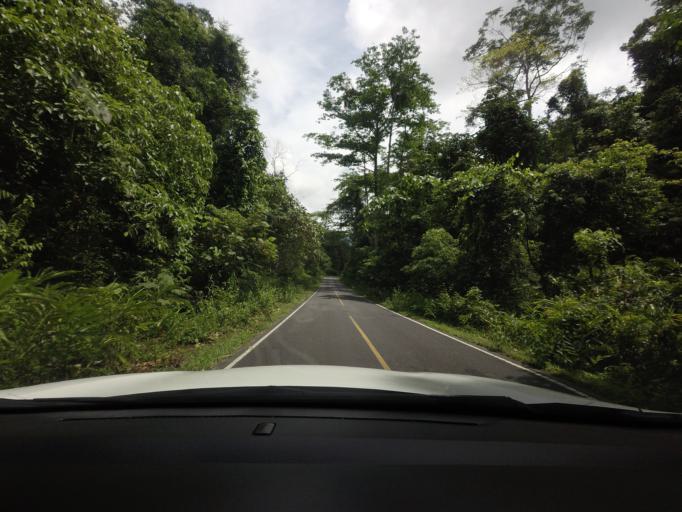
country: TH
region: Nakhon Nayok
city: Pak Phli
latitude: 14.2821
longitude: 101.3928
